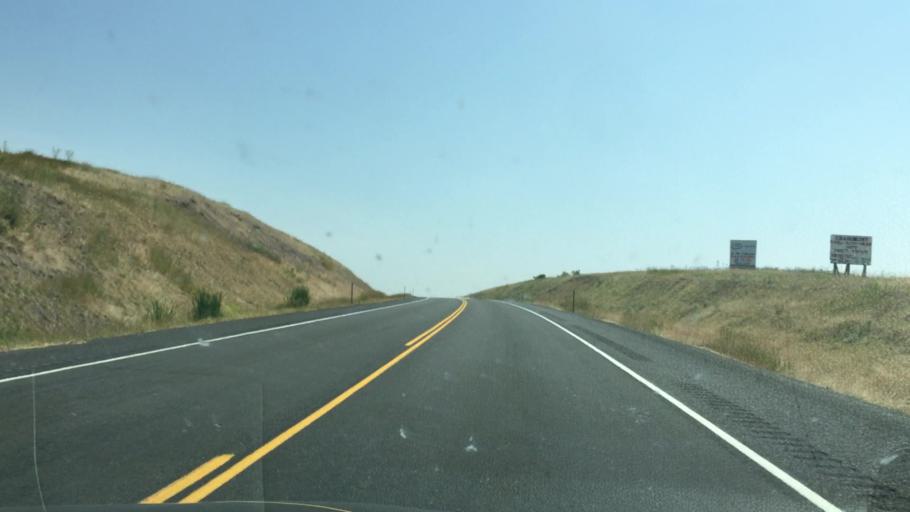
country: US
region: Idaho
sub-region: Lewis County
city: Nezperce
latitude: 46.2340
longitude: -116.5092
